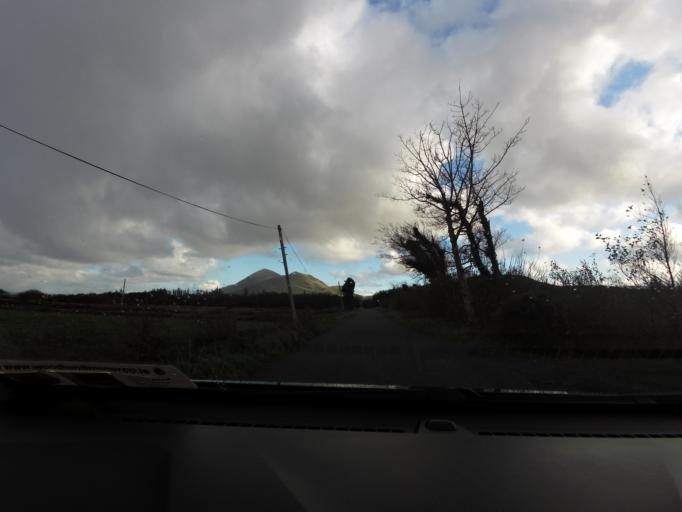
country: IE
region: Connaught
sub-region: Maigh Eo
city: Westport
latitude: 53.7735
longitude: -9.7700
